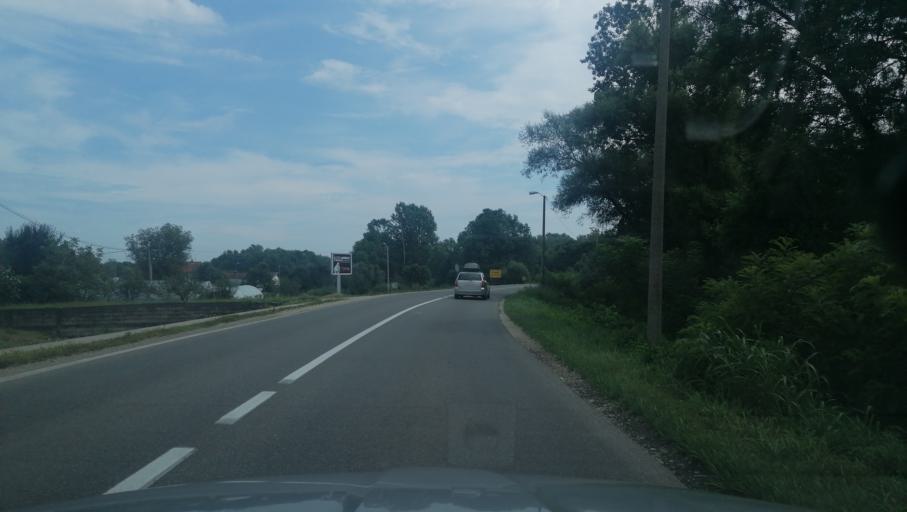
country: BA
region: Brcko
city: Brcko
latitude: 44.9263
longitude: 18.7317
